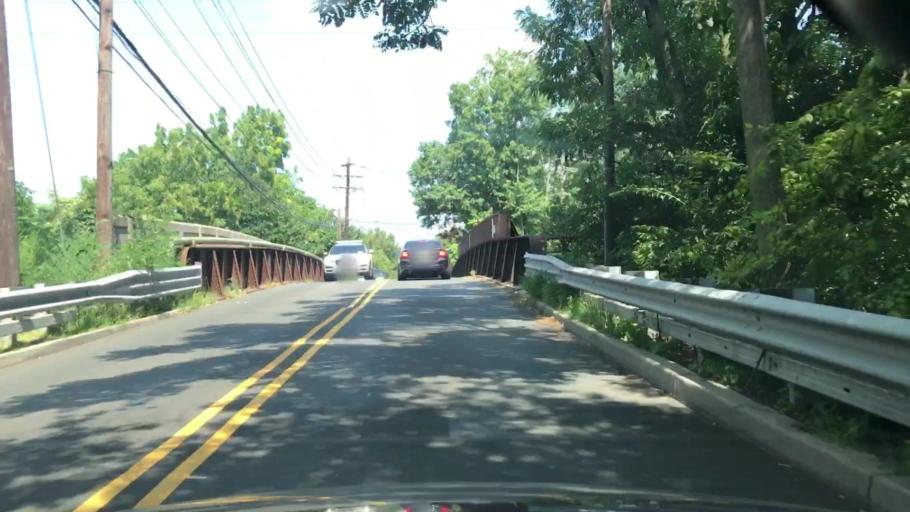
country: US
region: New Jersey
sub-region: Middlesex County
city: Metuchen
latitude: 40.5361
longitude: -74.3753
